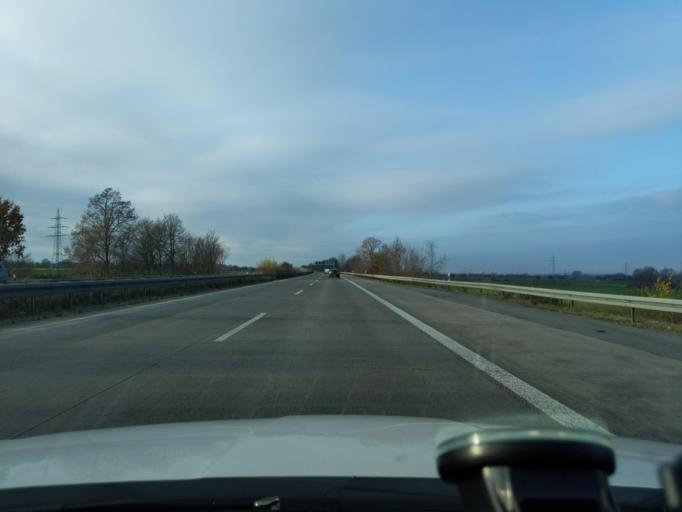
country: DE
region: North Rhine-Westphalia
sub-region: Regierungsbezirk Arnsberg
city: Soest
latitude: 51.5458
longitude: 8.0452
